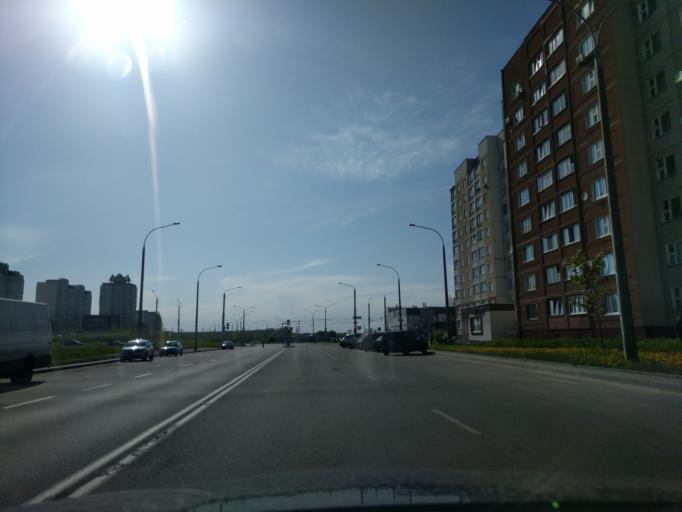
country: BY
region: Minsk
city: Novoye Medvezhino
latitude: 53.8960
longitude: 27.4251
